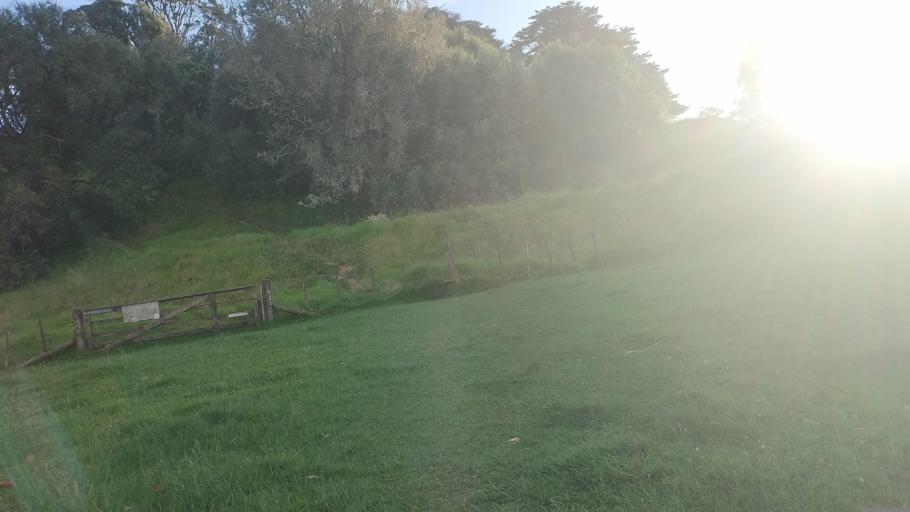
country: NZ
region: Auckland
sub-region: Auckland
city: Auckland
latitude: -36.8982
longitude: 174.7825
